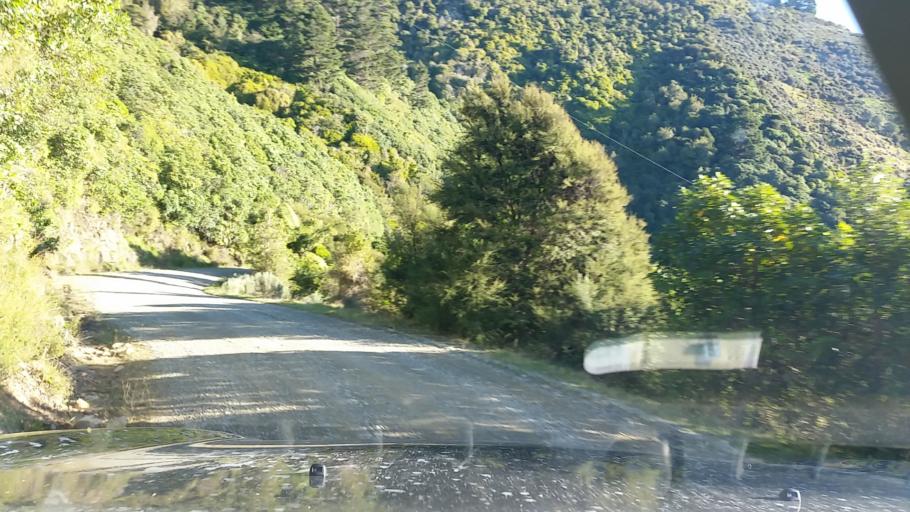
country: NZ
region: Marlborough
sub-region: Marlborough District
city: Picton
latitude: -41.0255
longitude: 174.1526
